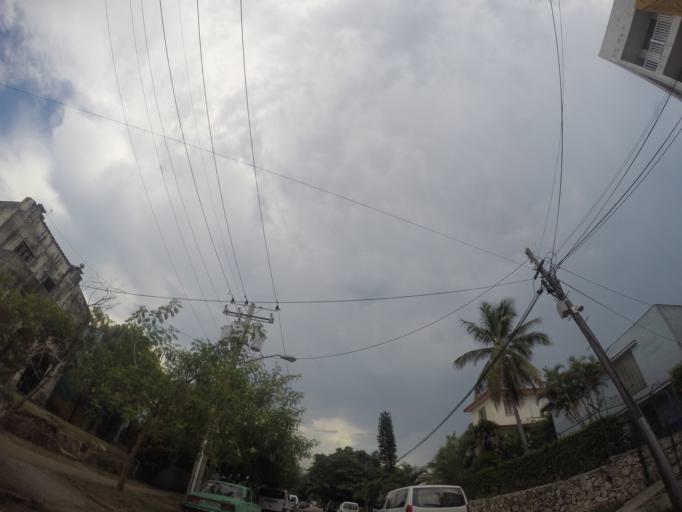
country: CU
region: La Habana
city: Havana
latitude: 23.1212
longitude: -82.4207
